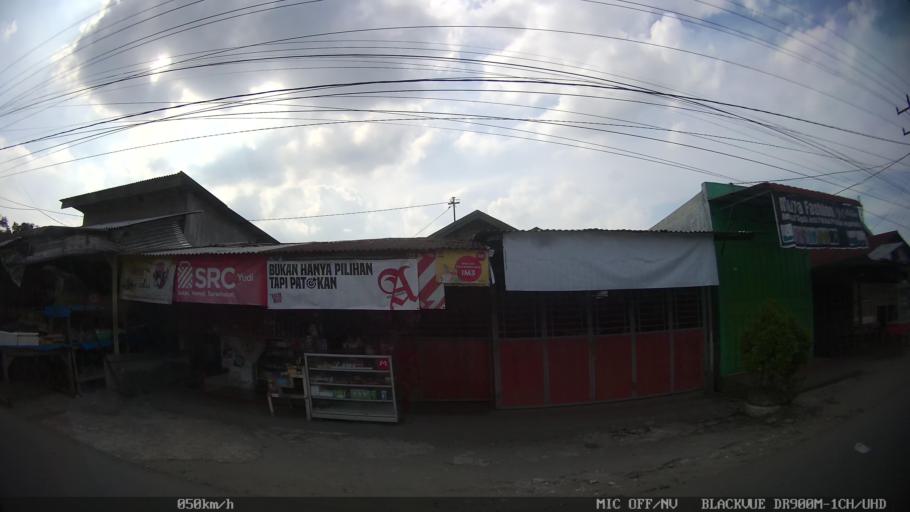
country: ID
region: North Sumatra
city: Binjai
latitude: 3.6425
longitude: 98.4968
